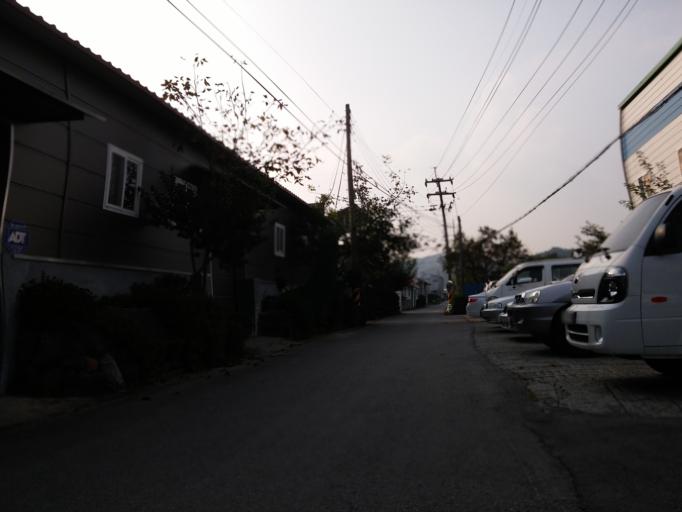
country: KR
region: Chungcheongbuk-do
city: Okcheon
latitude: 36.3323
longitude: 127.5290
